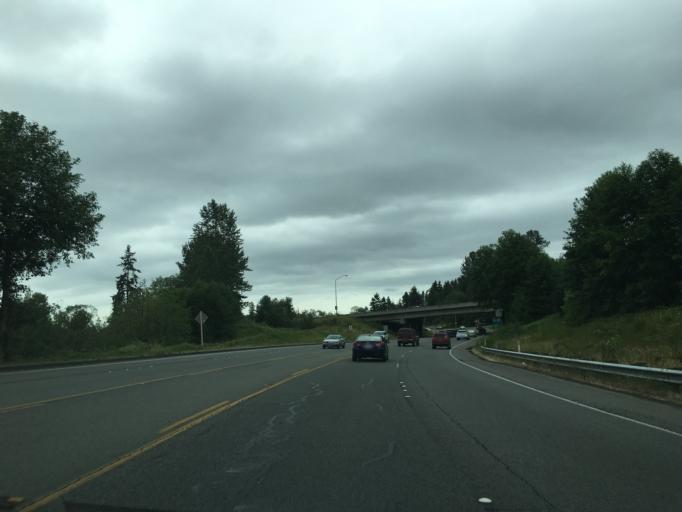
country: US
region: Washington
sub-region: Snohomish County
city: Alderwood Manor
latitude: 47.8406
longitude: -122.2712
